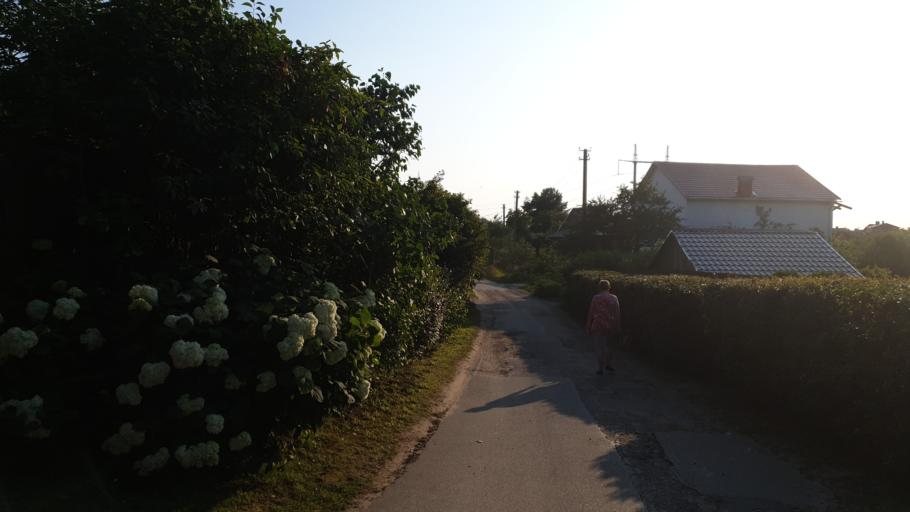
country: LT
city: Grigiskes
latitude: 54.7659
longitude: 25.0306
